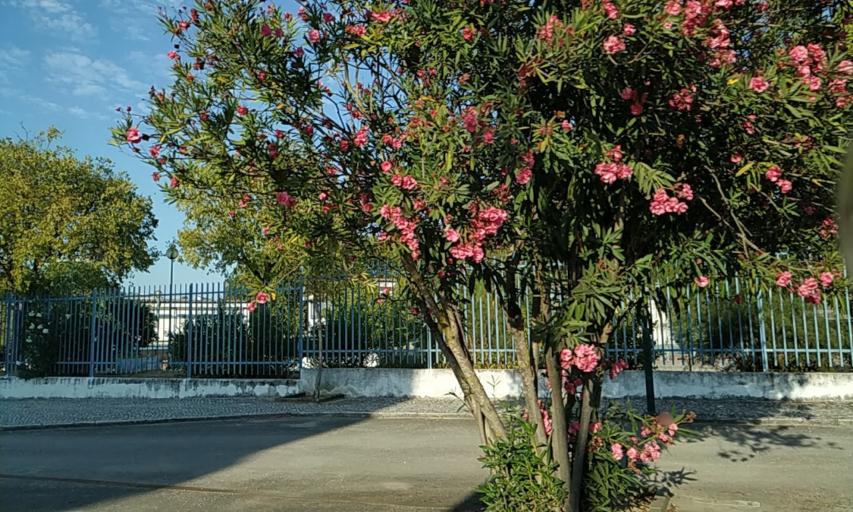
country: PT
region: Santarem
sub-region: Alcanena
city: Alcanena
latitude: 39.3779
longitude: -8.6609
